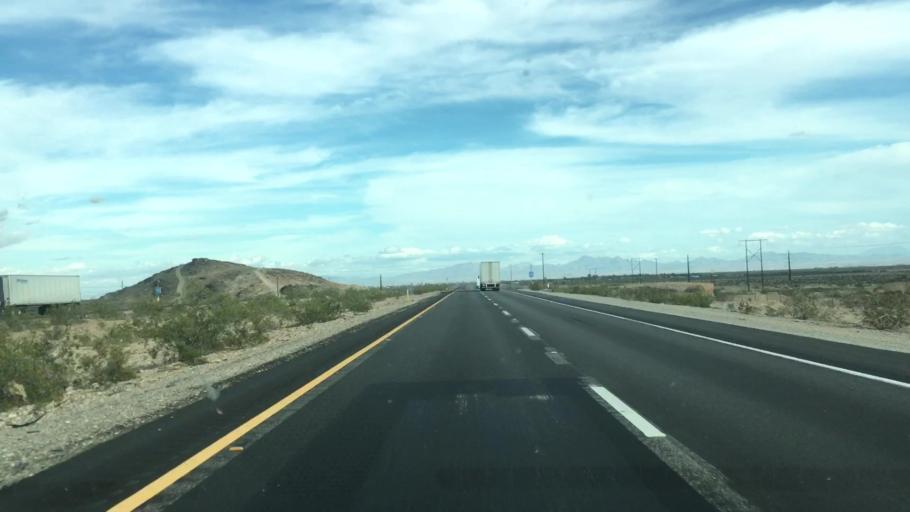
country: US
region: California
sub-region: Riverside County
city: Mesa Verde
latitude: 33.6087
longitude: -114.7654
